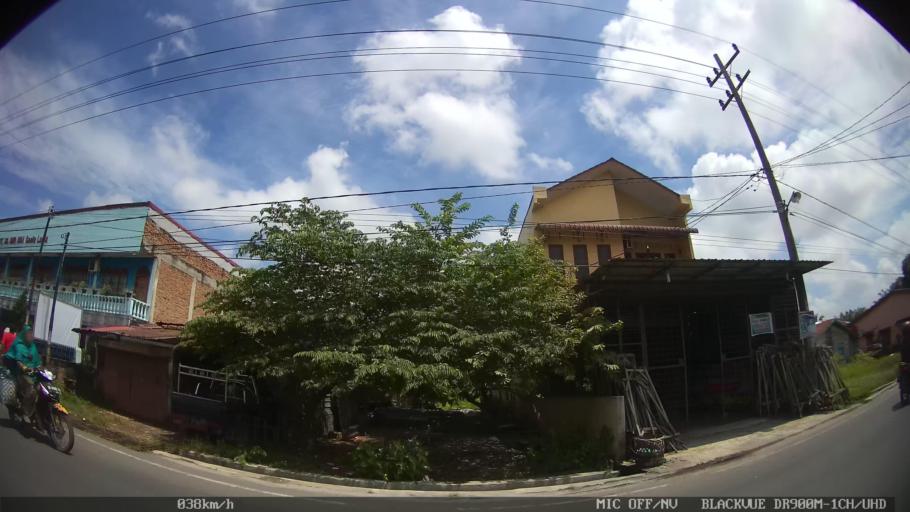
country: ID
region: North Sumatra
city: Percut
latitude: 3.6075
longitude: 98.7837
